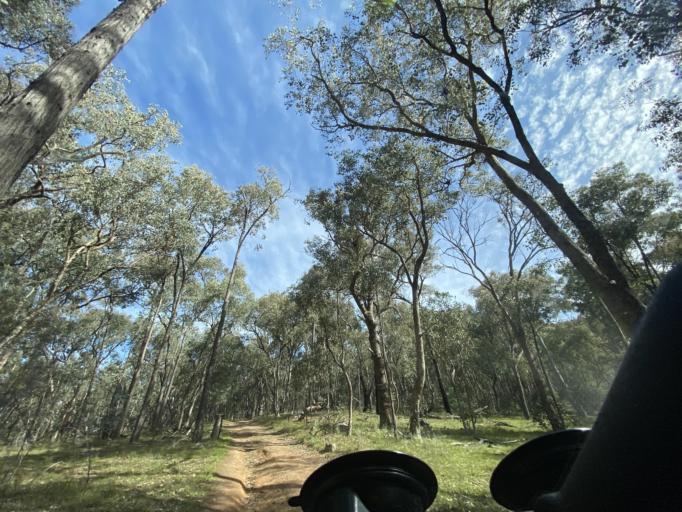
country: AU
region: Victoria
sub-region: Mansfield
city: Mansfield
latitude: -36.8037
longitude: 146.1192
